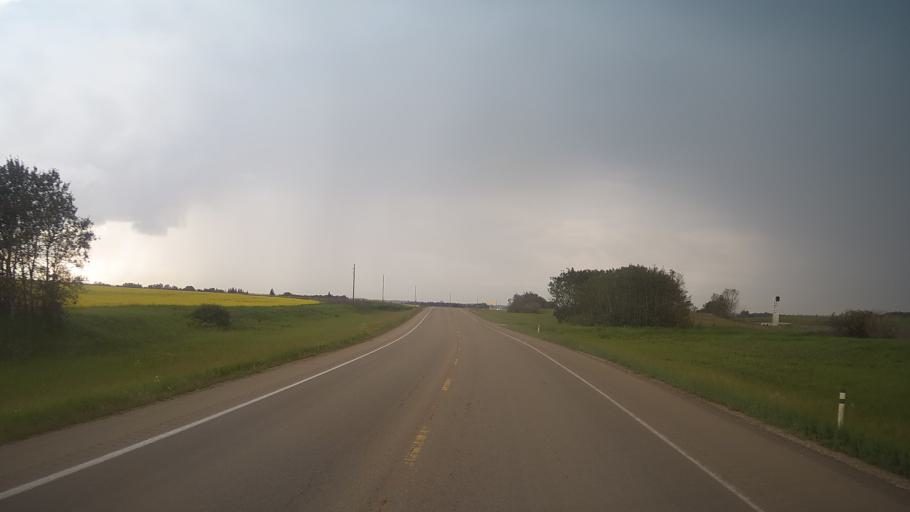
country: CA
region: Alberta
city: Tofield
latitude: 53.3222
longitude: -112.5472
